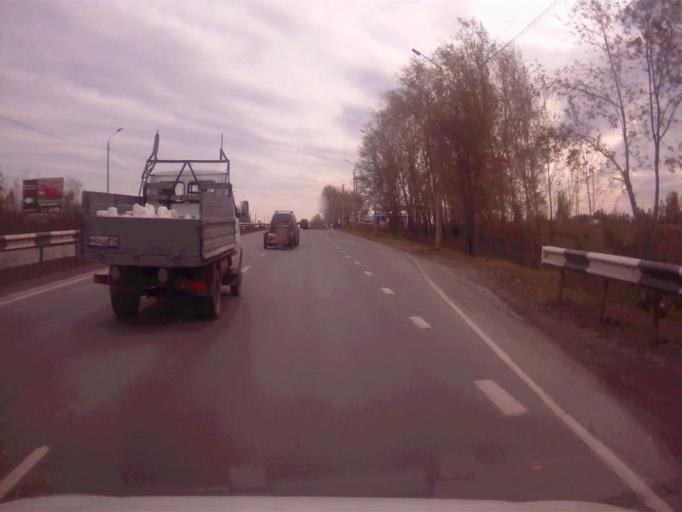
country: RU
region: Chelyabinsk
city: Novosineglazovskiy
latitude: 55.0568
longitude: 61.4059
